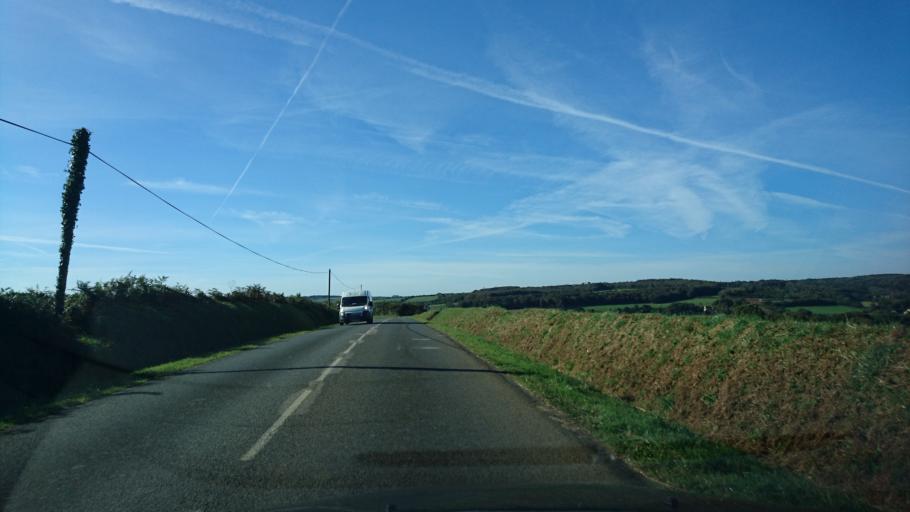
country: FR
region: Brittany
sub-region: Departement du Finistere
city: Saint-Renan
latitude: 48.4302
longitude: -4.6354
